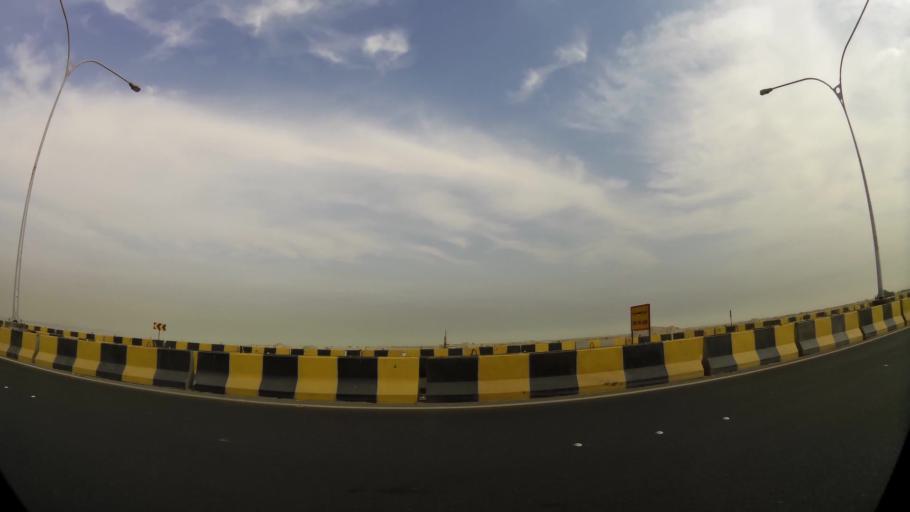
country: KW
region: Al Asimah
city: Ar Rabiyah
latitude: 29.3198
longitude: 47.8389
